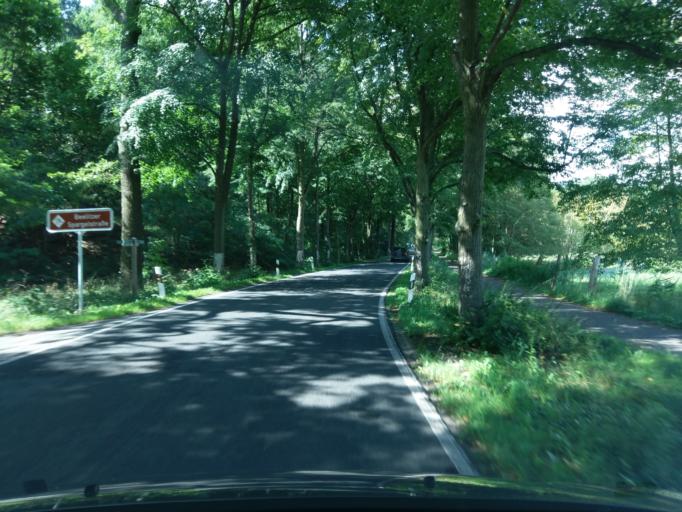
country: DE
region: Brandenburg
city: Borkwalde
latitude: 52.3026
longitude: 12.7684
